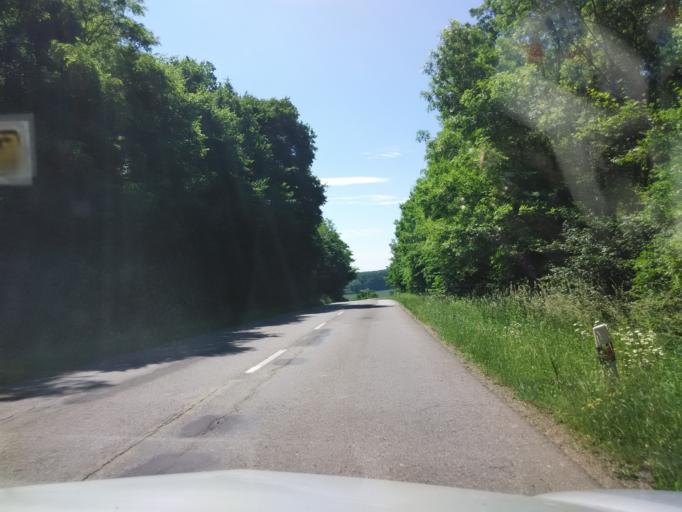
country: SK
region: Nitriansky
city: Tlmace
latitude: 48.2489
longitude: 18.4576
